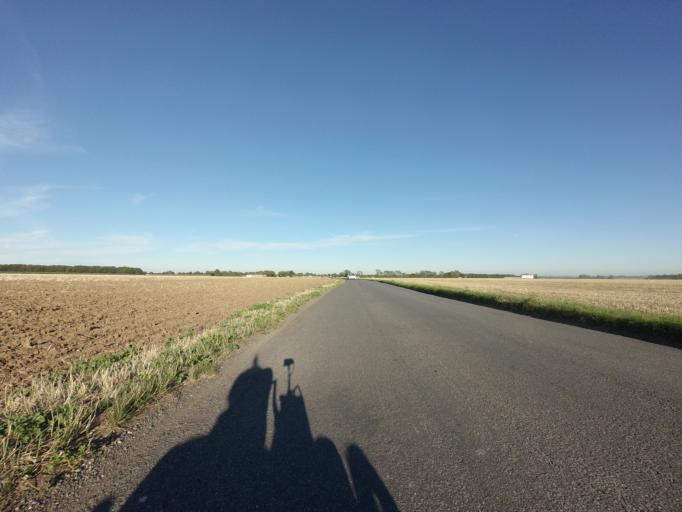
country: GB
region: England
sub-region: Kent
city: Herne Bay
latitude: 51.3565
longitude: 1.1620
